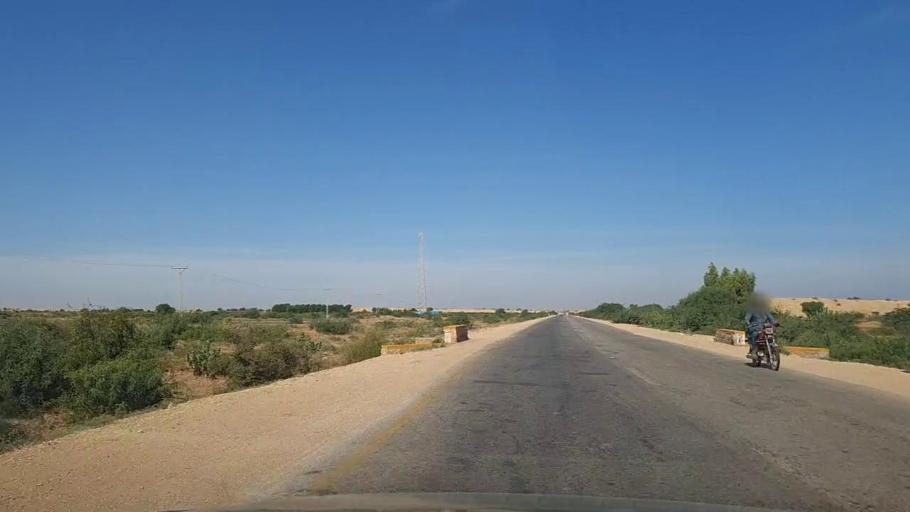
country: PK
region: Sindh
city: Kotri
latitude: 25.2022
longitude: 68.2374
